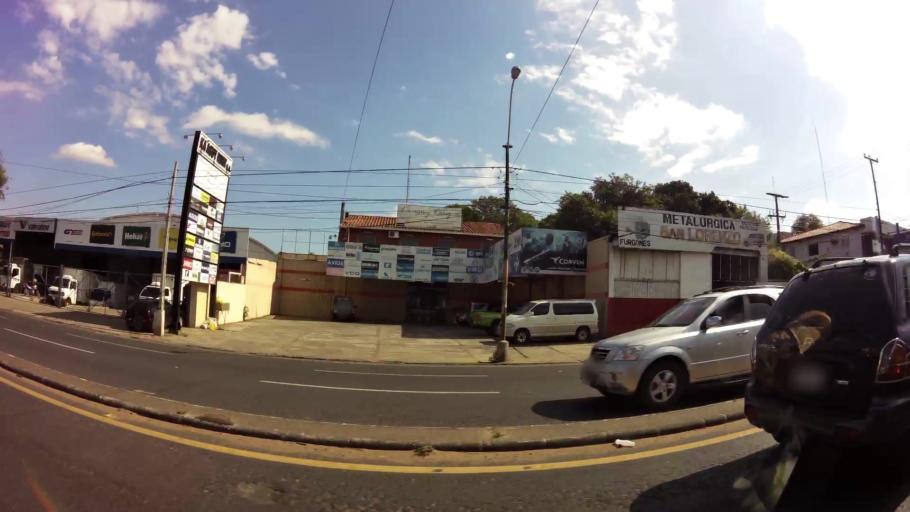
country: PY
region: Central
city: Fernando de la Mora
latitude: -25.3360
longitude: -57.5314
